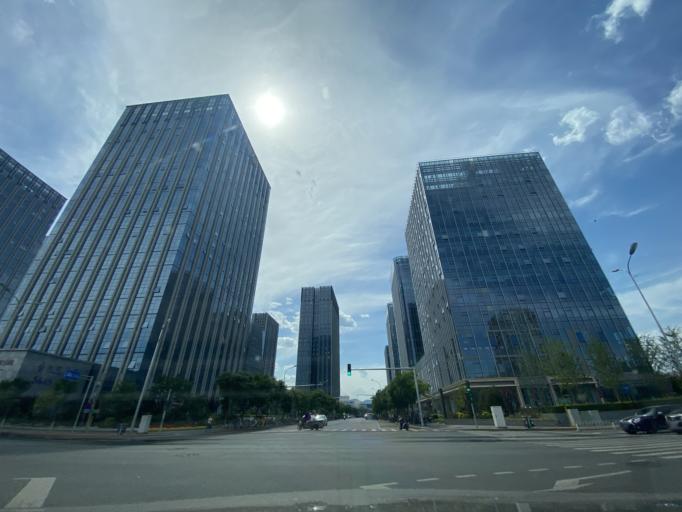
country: CN
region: Beijing
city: Lugu
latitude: 39.9046
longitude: 116.1805
